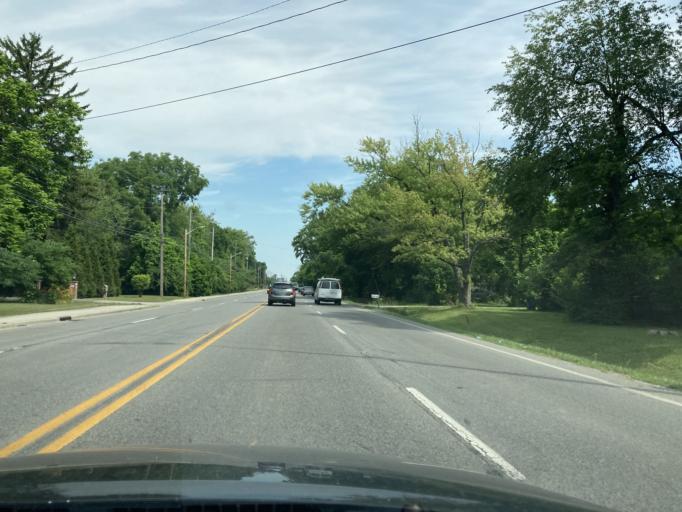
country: US
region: Indiana
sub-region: Marion County
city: Meridian Hills
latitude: 39.8739
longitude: -86.2045
